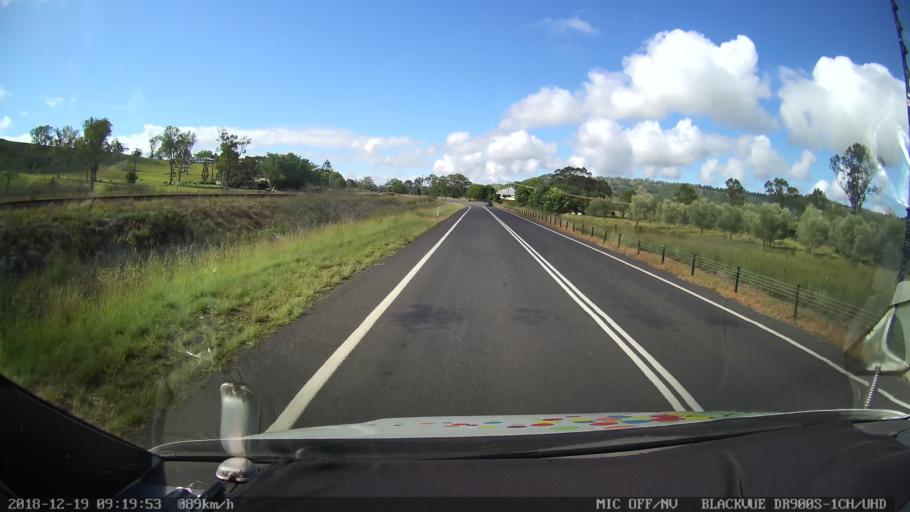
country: AU
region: New South Wales
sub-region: Kyogle
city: Kyogle
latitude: -28.5658
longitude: 152.9780
